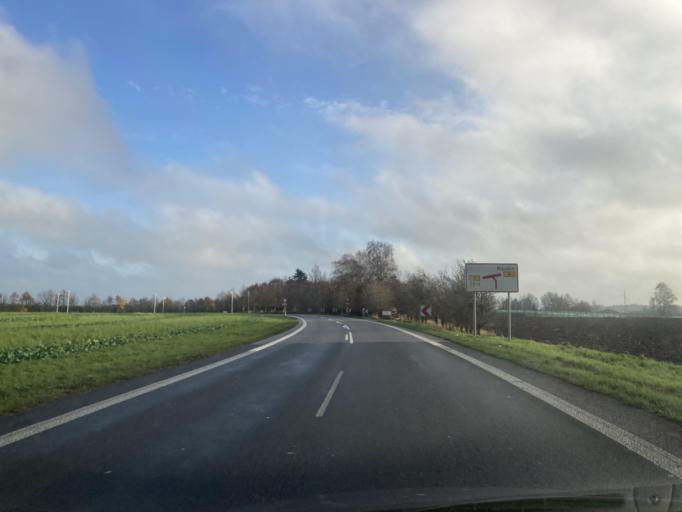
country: DK
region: Zealand
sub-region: Lolland Kommune
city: Maribo
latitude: 54.8134
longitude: 11.4017
